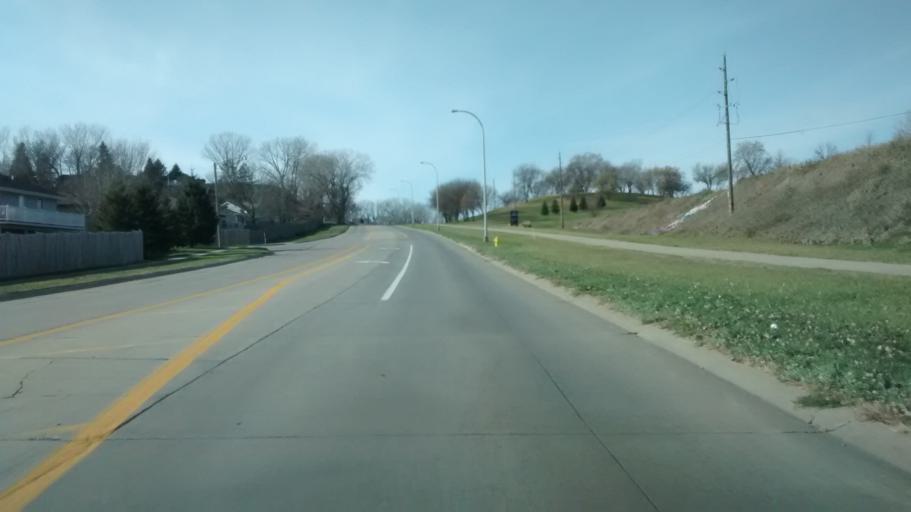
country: US
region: Iowa
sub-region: Woodbury County
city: Sioux City
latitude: 42.5411
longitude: -96.3887
